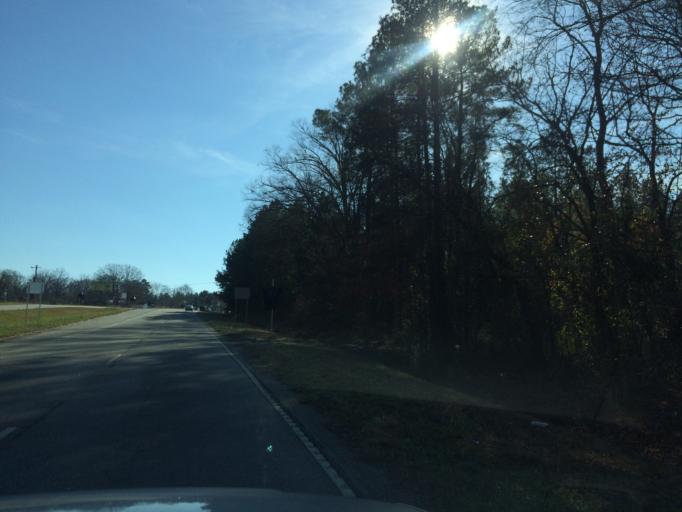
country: US
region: South Carolina
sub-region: Greenwood County
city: Greenwood
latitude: 34.2395
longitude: -82.1017
